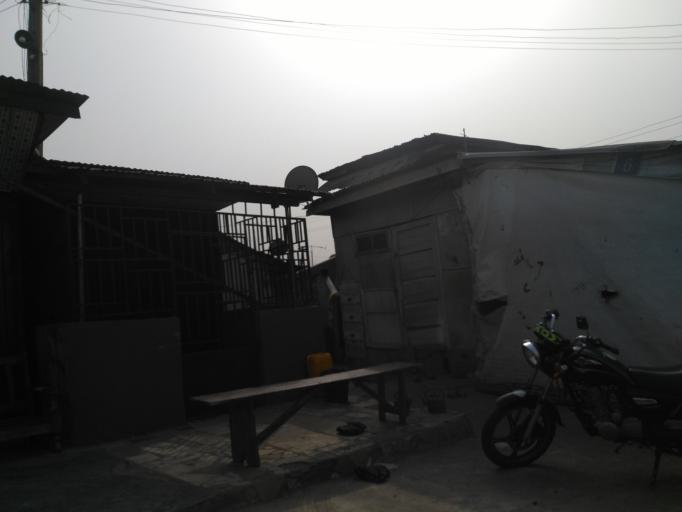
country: GH
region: Ashanti
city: Kumasi
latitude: 6.6980
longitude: -1.6062
